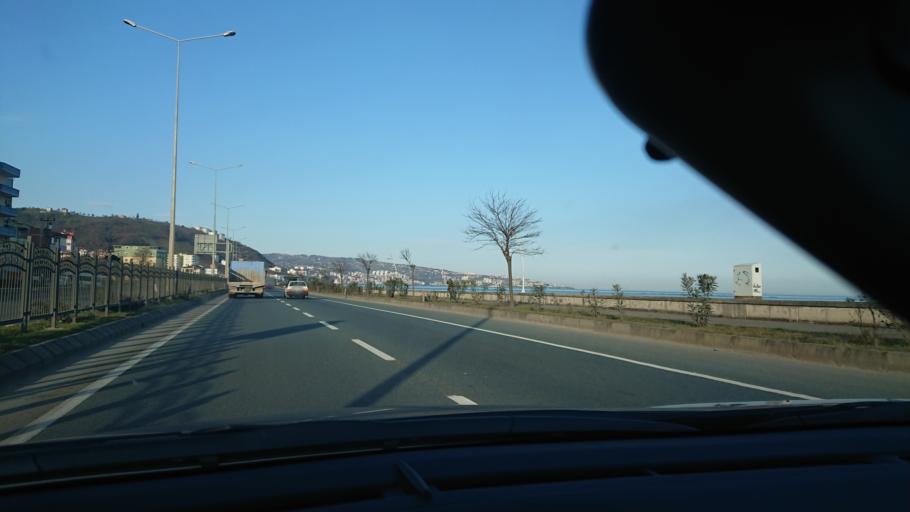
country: TR
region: Trabzon
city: Arsin
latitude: 40.9545
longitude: 39.9193
